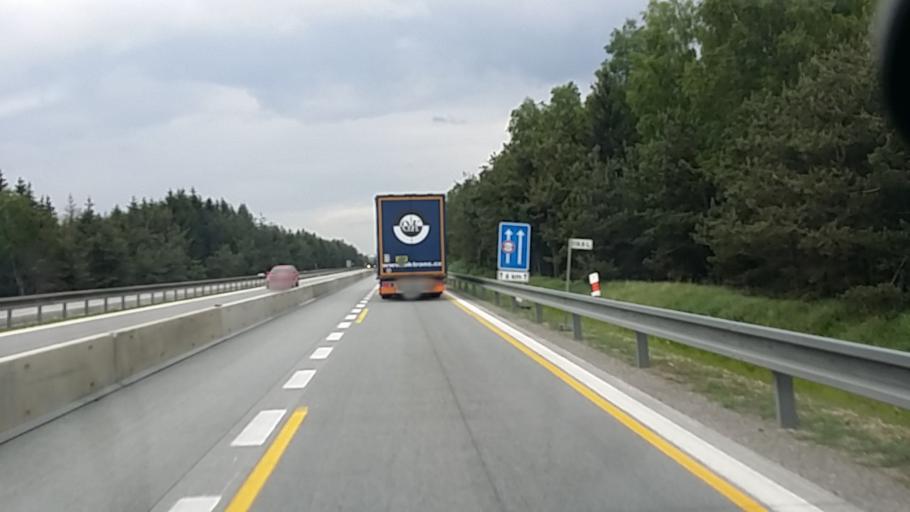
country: CZ
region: Vysocina
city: Velky Beranov
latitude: 49.4235
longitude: 15.6832
